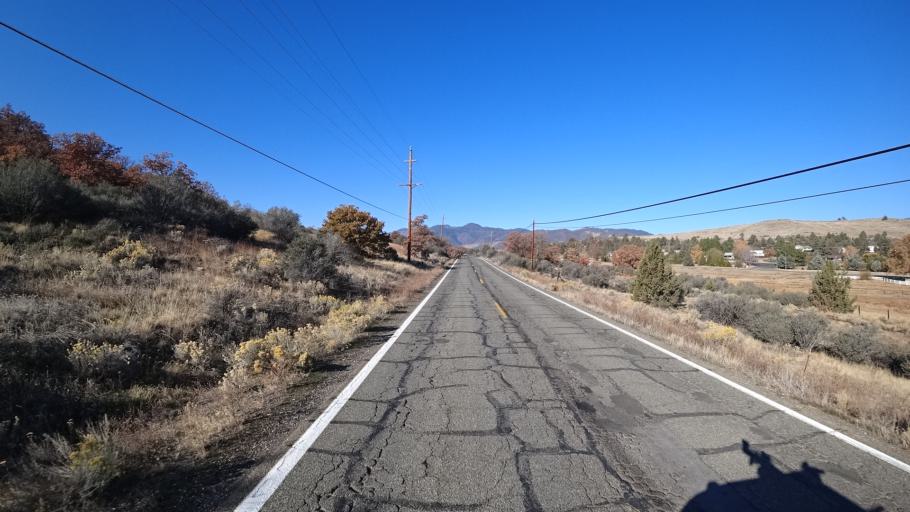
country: US
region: California
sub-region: Siskiyou County
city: Yreka
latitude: 41.7389
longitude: -122.6099
